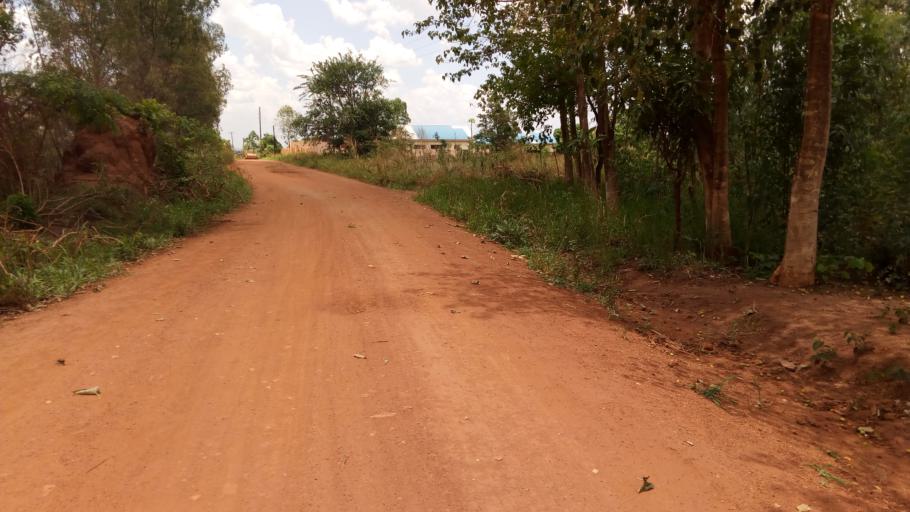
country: UG
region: Northern Region
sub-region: Gulu District
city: Gulu
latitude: 2.7905
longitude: 32.3491
